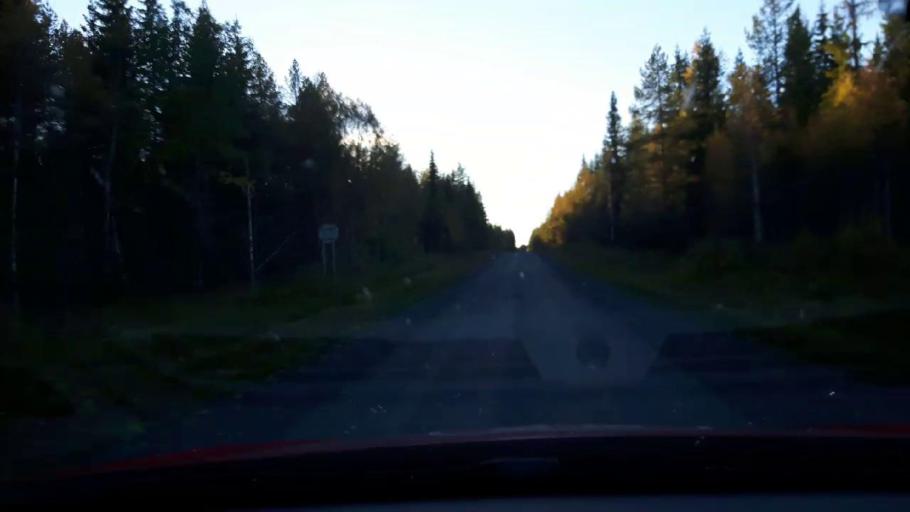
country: SE
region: Jaemtland
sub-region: OEstersunds Kommun
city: Lit
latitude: 63.4119
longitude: 14.6457
